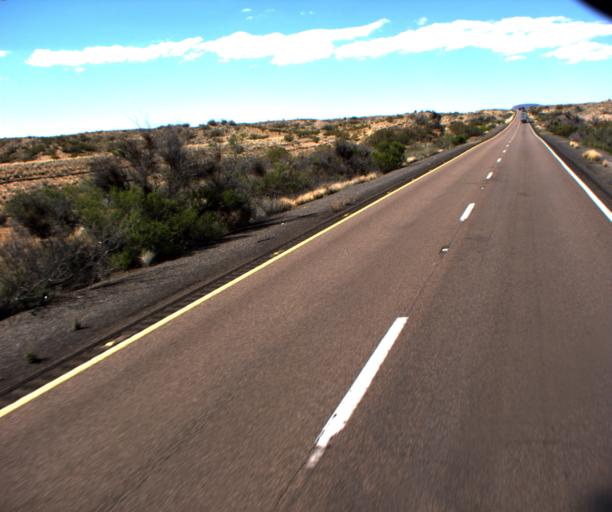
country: US
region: Arizona
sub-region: Mohave County
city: Kingman
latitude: 35.0608
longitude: -113.6649
